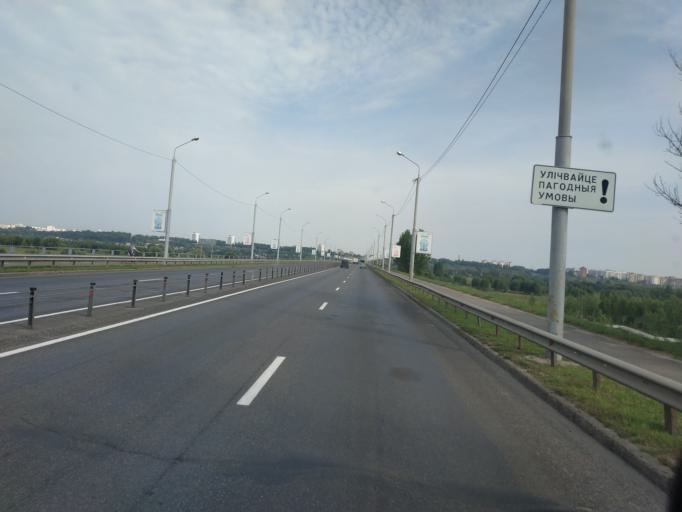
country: BY
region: Mogilev
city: Mahilyow
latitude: 53.8857
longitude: 30.3790
